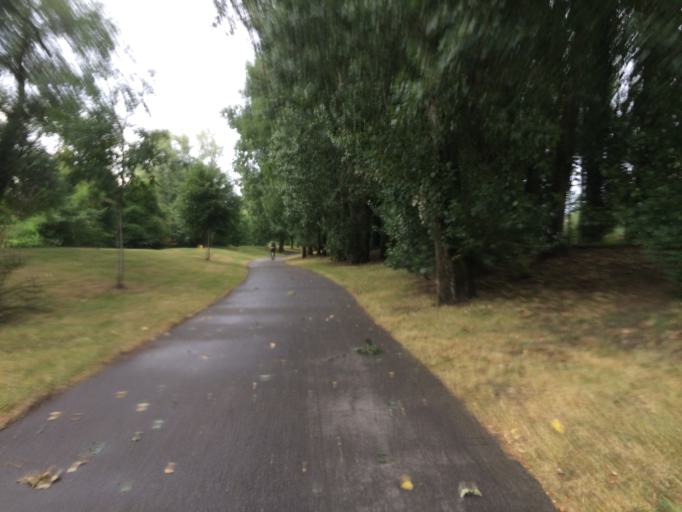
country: FR
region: Picardie
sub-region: Departement de l'Oise
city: Venette
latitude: 49.4064
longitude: 2.7979
